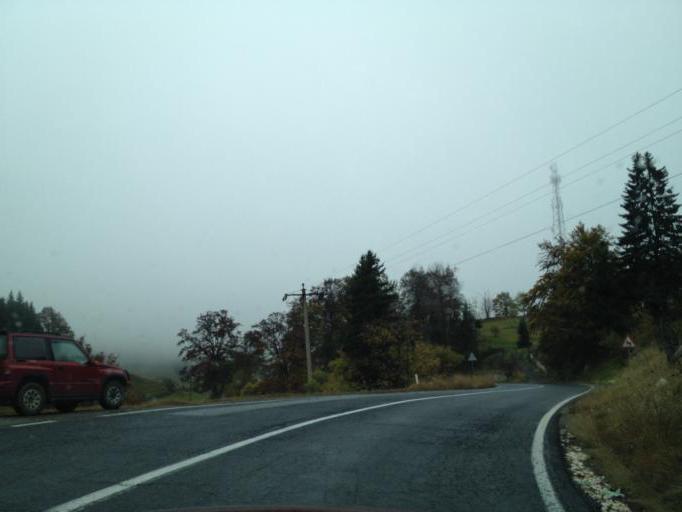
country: RO
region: Brasov
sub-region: Comuna Fundata
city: Fundata
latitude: 45.4453
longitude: 25.2777
